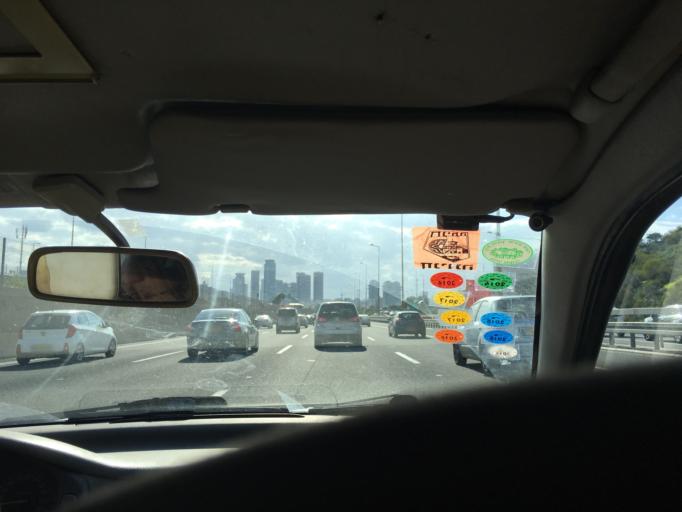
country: IL
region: Tel Aviv
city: Ramat Gan
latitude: 32.1082
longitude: 34.8073
